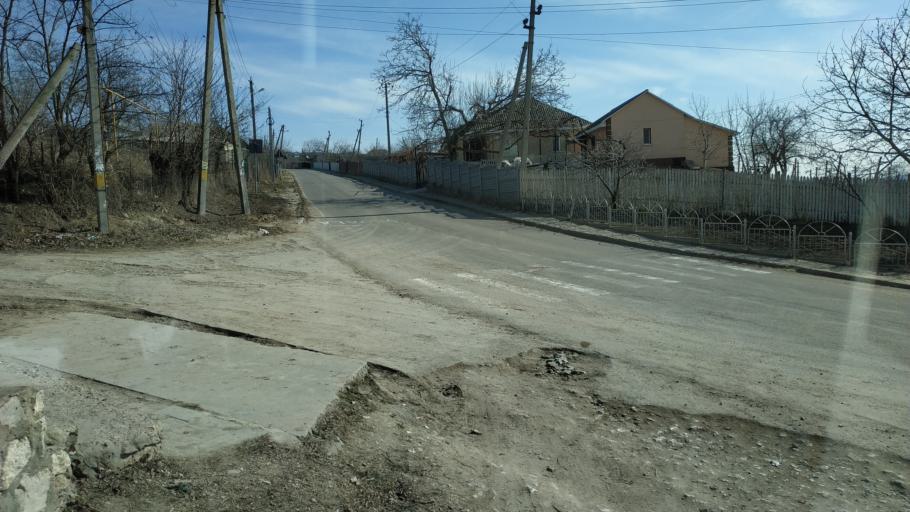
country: MD
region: Nisporeni
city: Nisporeni
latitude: 47.2253
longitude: 28.0401
